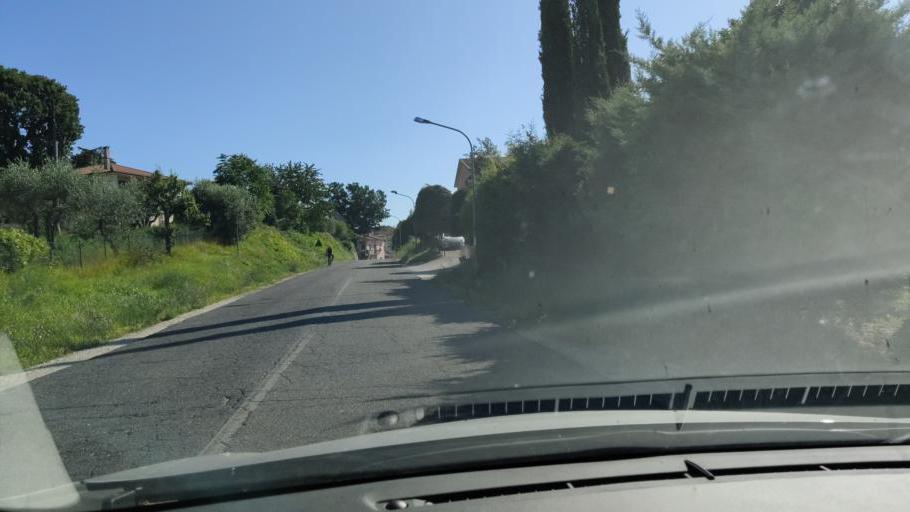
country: IT
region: Umbria
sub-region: Provincia di Terni
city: Avigliano Umbro
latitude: 42.6533
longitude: 12.4219
